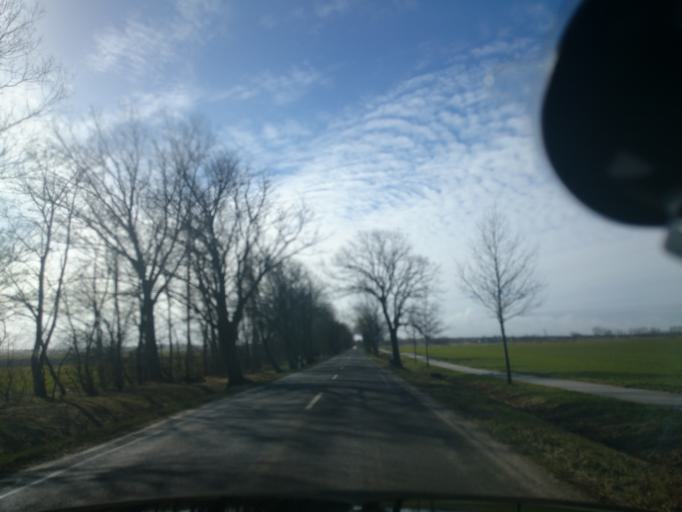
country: DE
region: Mecklenburg-Vorpommern
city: Elmenhorst
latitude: 54.1650
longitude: 12.0349
